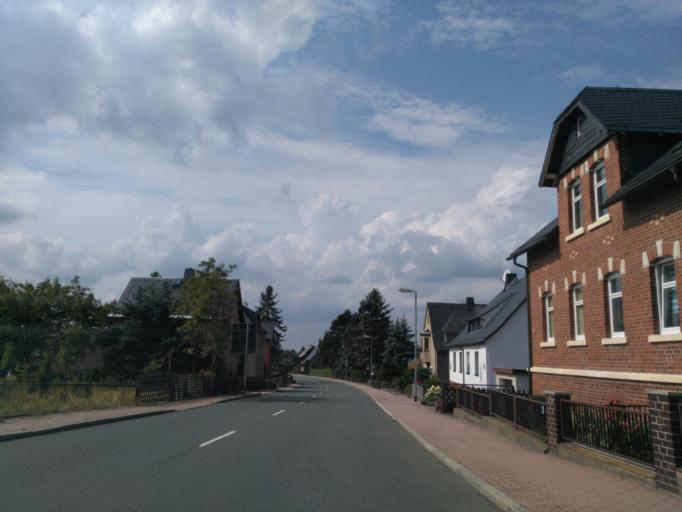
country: DE
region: Saxony
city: Stutzengrun
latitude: 50.5359
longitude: 12.5070
